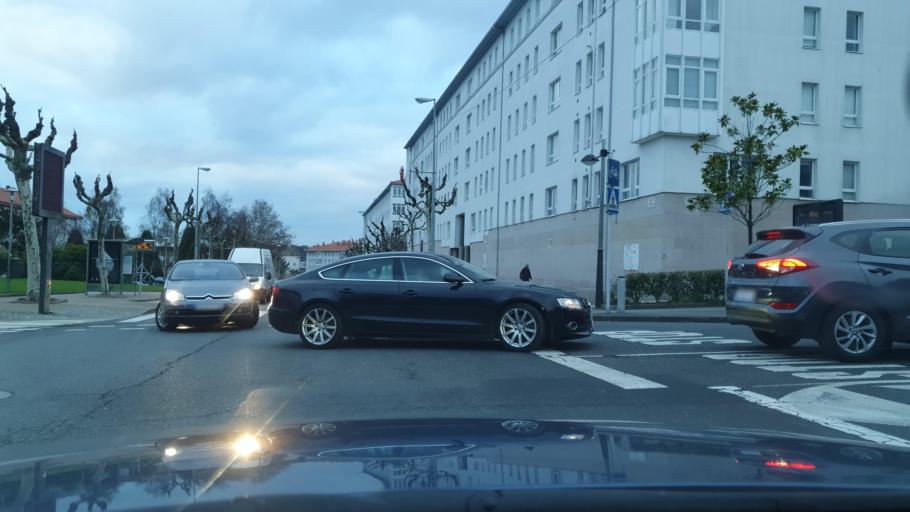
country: ES
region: Galicia
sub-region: Provincia da Coruna
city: Santiago de Compostela
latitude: 42.8832
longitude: -8.5294
